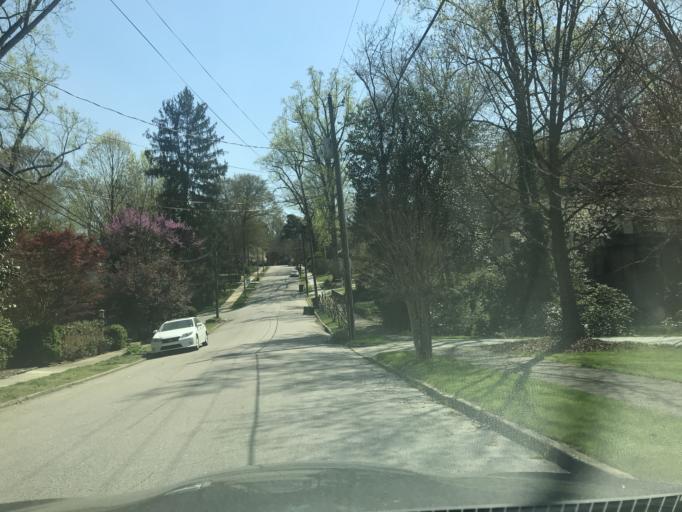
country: US
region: North Carolina
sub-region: Wake County
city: West Raleigh
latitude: 35.8138
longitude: -78.6426
